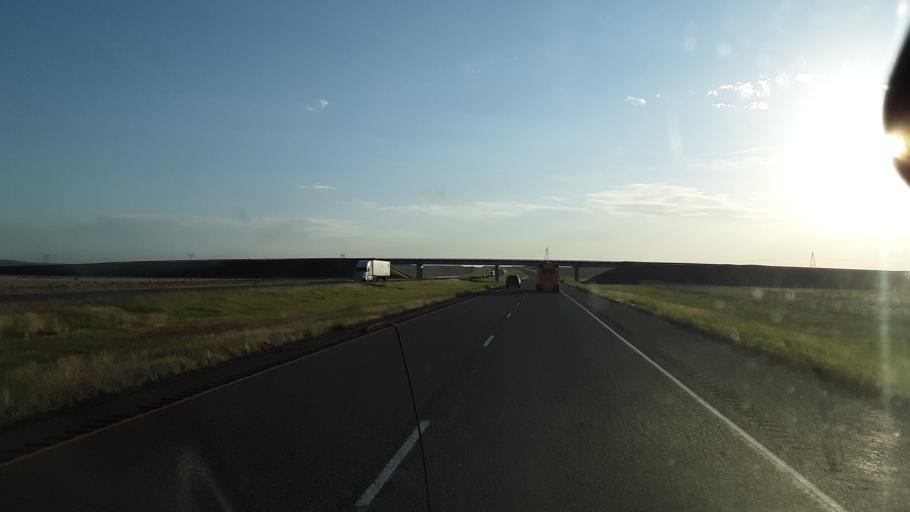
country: US
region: Montana
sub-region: Big Horn County
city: Hardin
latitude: 45.7463
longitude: -107.6783
